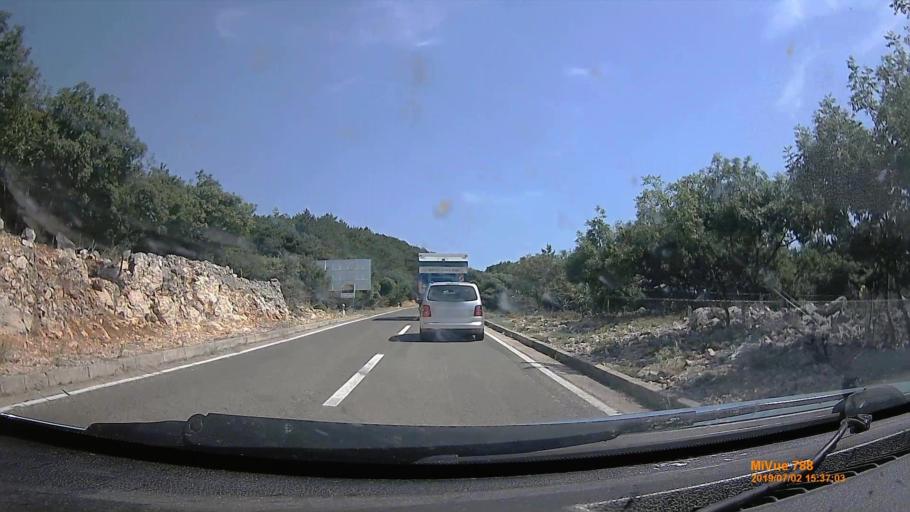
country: HR
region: Primorsko-Goranska
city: Cres
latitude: 44.9809
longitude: 14.4142
